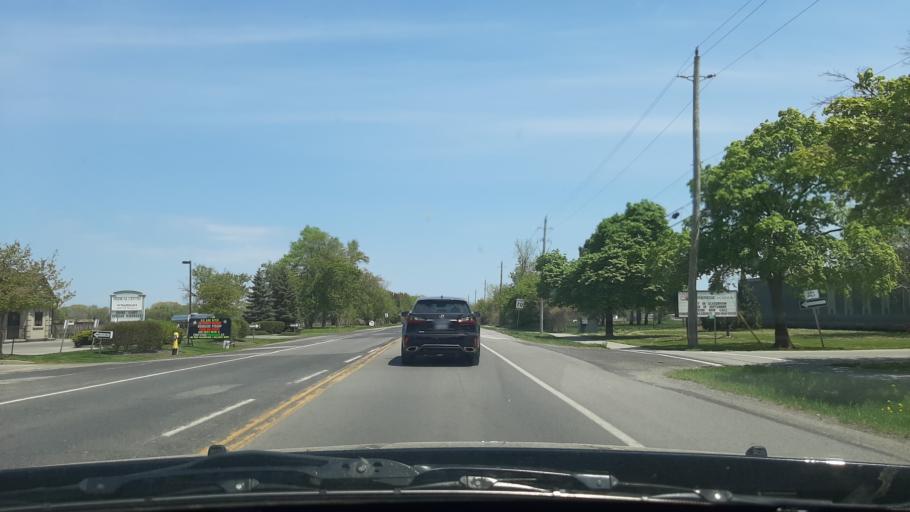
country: US
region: New York
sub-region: Niagara County
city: Youngstown
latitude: 43.2352
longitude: -79.1055
